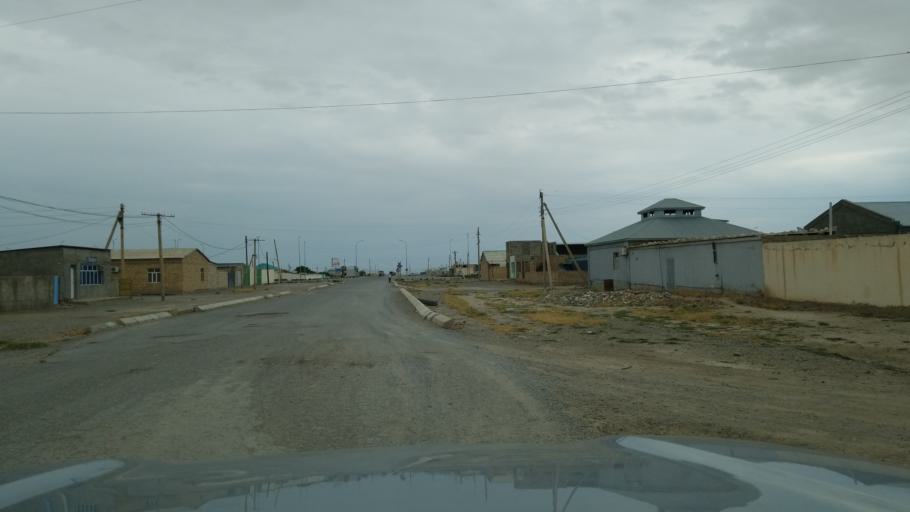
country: TM
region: Balkan
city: Serdar
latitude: 38.9936
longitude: 56.2787
